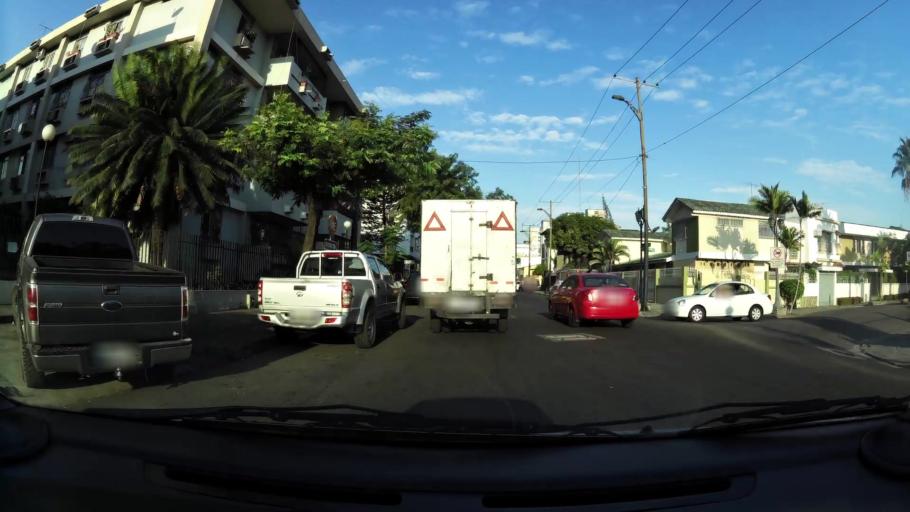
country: EC
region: Guayas
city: Guayaquil
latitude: -2.2159
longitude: -79.8896
